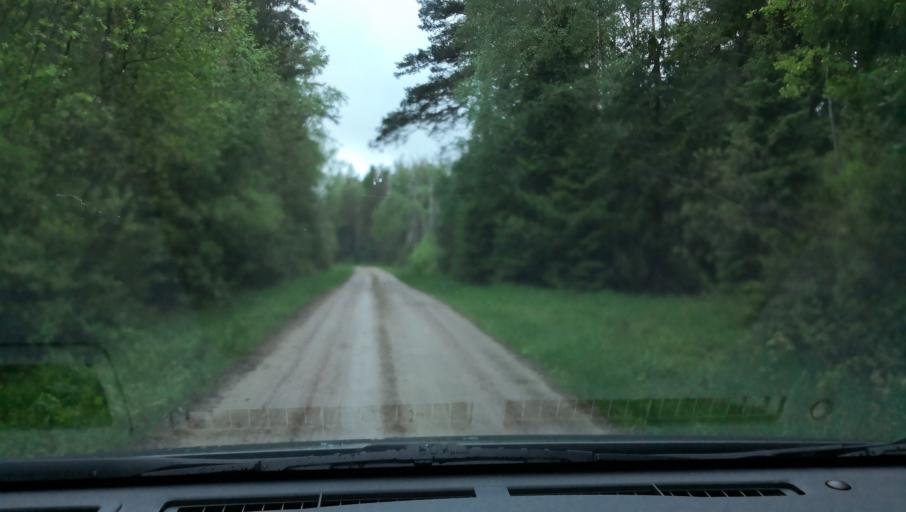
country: SE
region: Uppsala
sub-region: Enkopings Kommun
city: Orsundsbro
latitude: 59.9257
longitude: 17.3369
